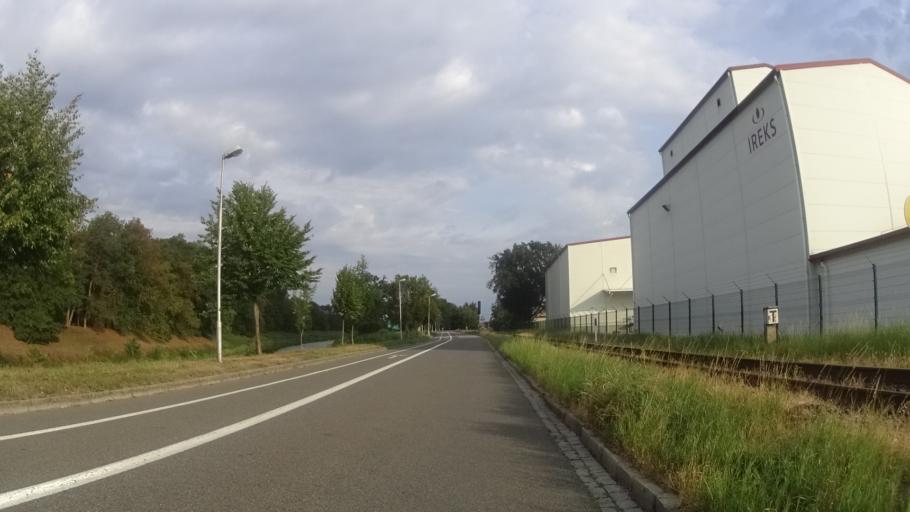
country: CZ
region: Zlin
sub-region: Okres Kromeriz
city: Kromeriz
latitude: 49.3050
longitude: 17.3979
